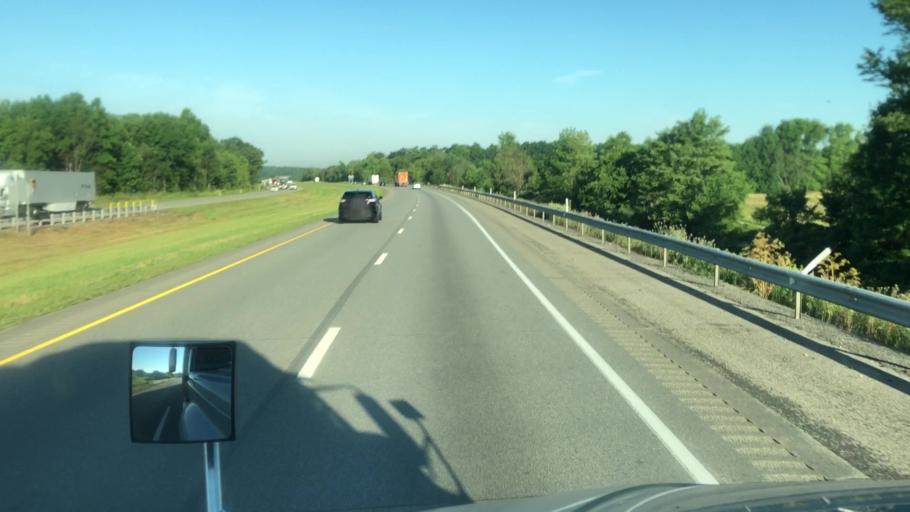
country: US
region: Pennsylvania
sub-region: Lawrence County
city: New Wilmington
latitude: 41.1858
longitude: -80.3647
